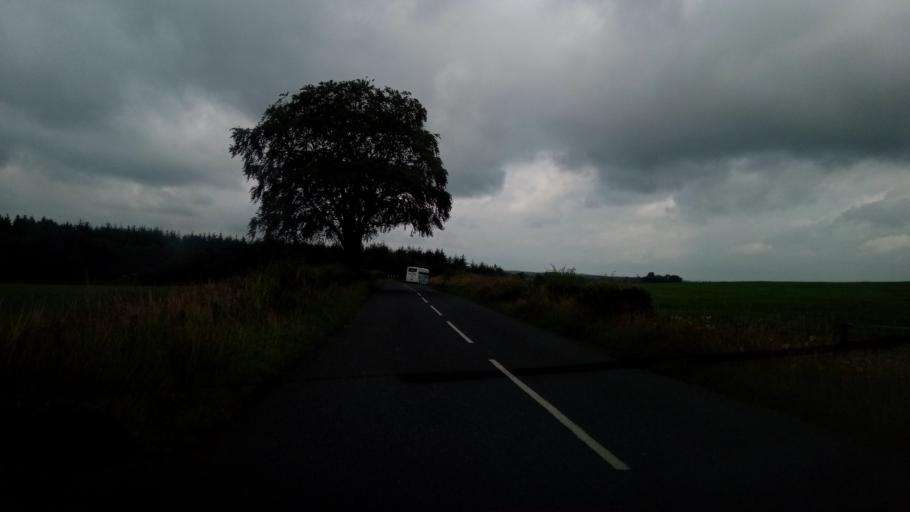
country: GB
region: Scotland
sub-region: Dumfries and Galloway
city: Langholm
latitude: 55.0910
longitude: -2.9053
